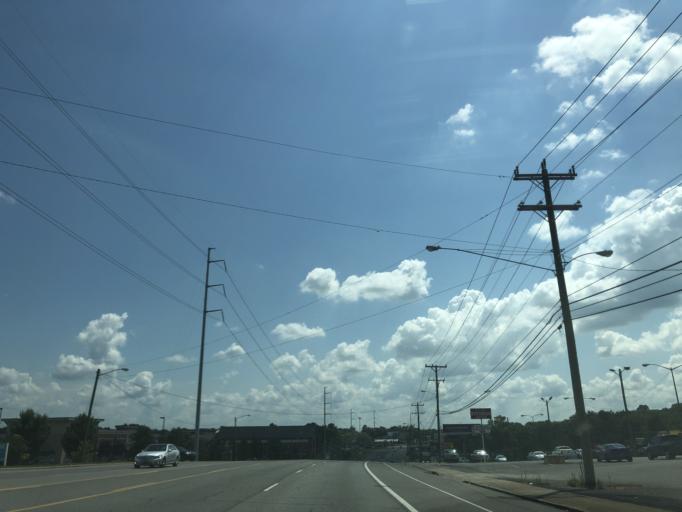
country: US
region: Tennessee
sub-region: Davidson County
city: Lakewood
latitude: 36.1952
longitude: -86.6220
